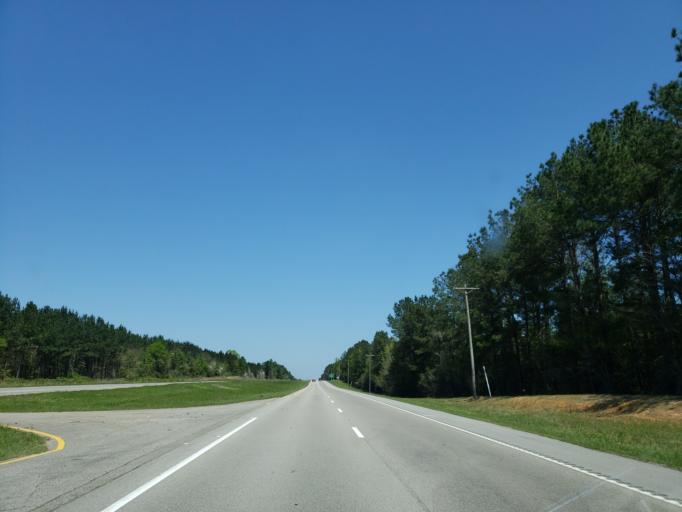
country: US
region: Mississippi
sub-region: Stone County
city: Wiggins
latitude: 31.0173
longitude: -89.2018
